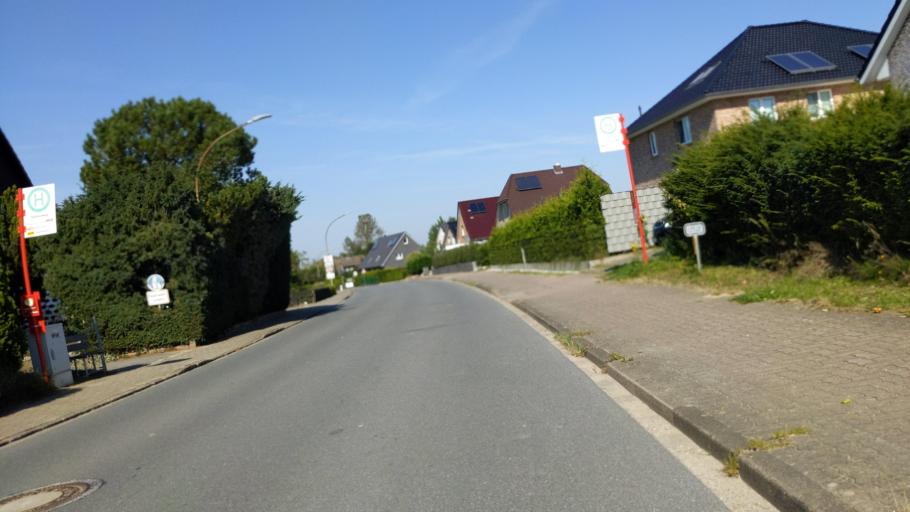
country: DE
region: Schleswig-Holstein
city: Meddewade
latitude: 53.8110
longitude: 10.4409
